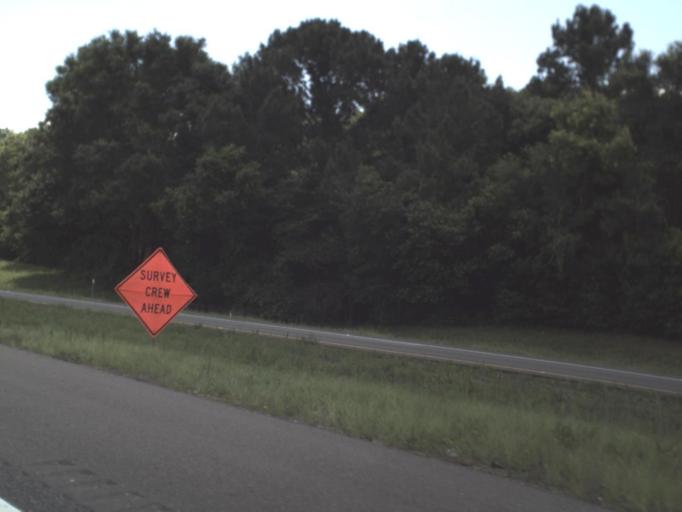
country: US
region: Florida
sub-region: Duval County
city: Jacksonville
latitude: 30.4461
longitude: -81.6096
